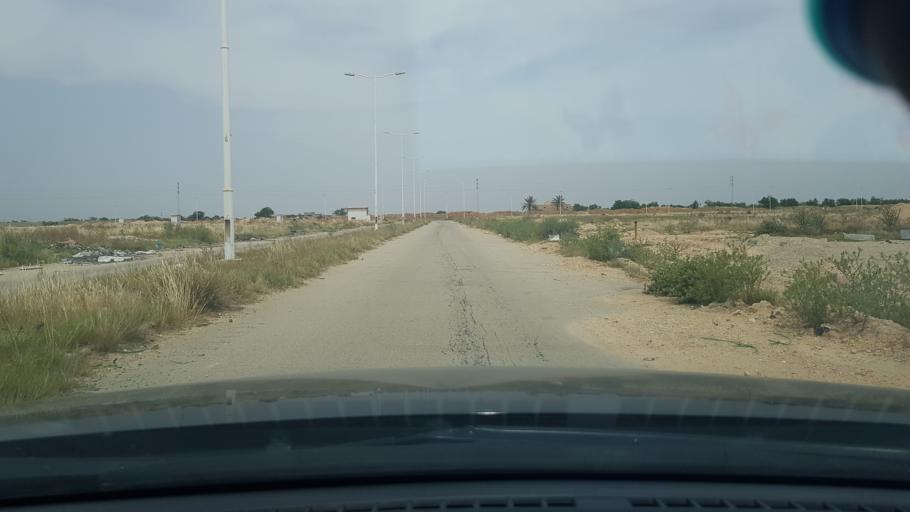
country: TN
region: Safaqis
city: Al Qarmadah
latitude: 34.8291
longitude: 10.7438
